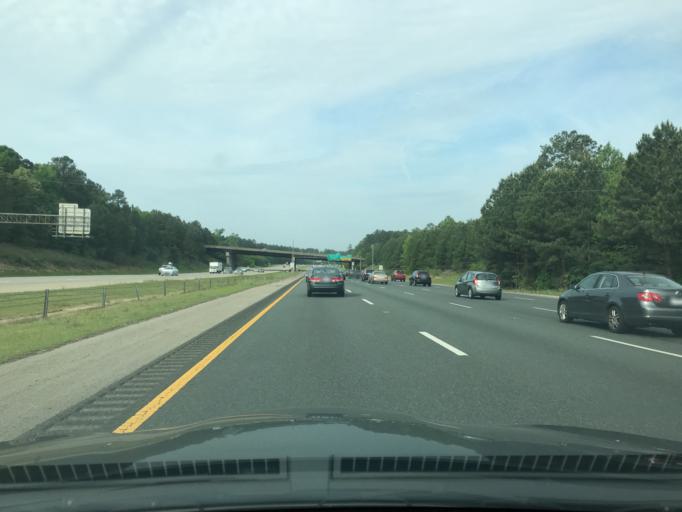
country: US
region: North Carolina
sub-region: Wake County
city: Morrisville
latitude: 35.9003
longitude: -78.7817
